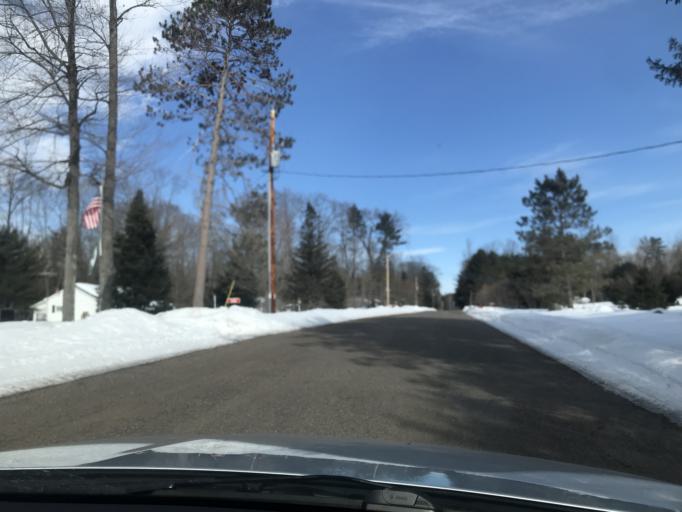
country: US
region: Wisconsin
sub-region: Oconto County
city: Gillett
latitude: 45.1212
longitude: -88.4193
